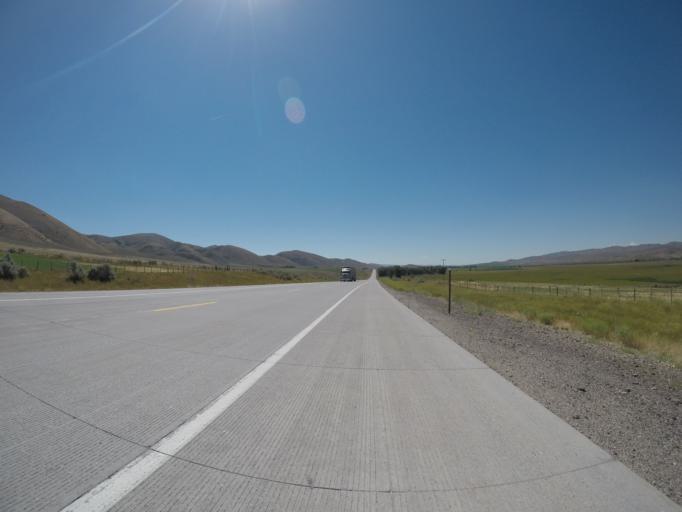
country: US
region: Idaho
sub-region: Bear Lake County
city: Montpelier
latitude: 42.1711
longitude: -110.9931
